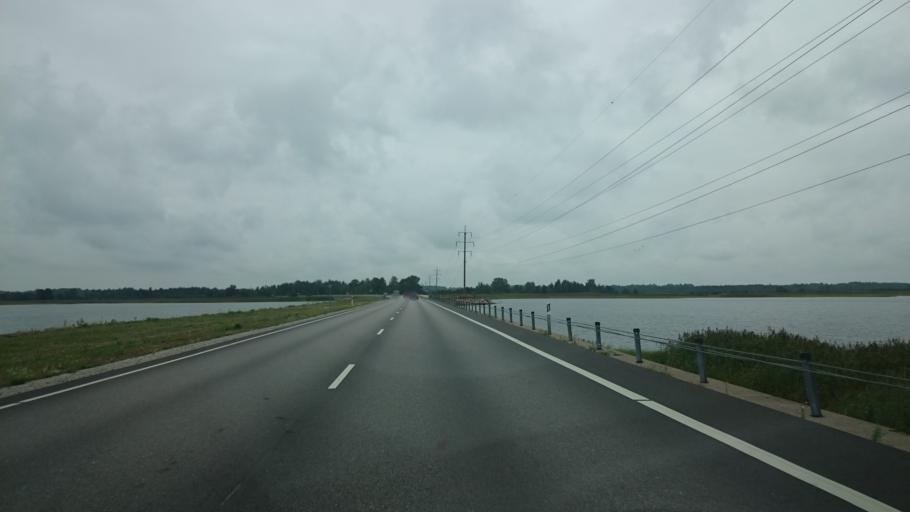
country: EE
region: Saare
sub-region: Orissaare vald
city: Orissaare
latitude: 58.5657
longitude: 23.1609
